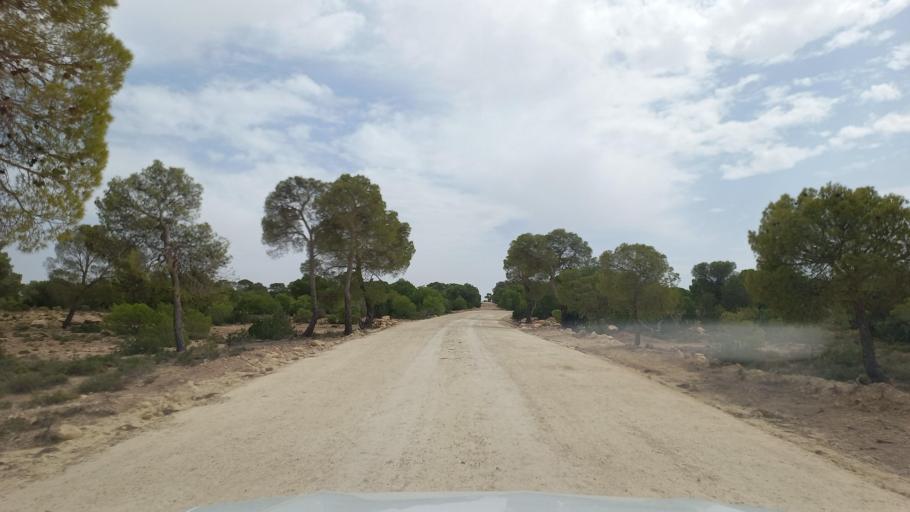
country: TN
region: Al Qasrayn
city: Kasserine
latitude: 35.3804
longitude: 8.8689
